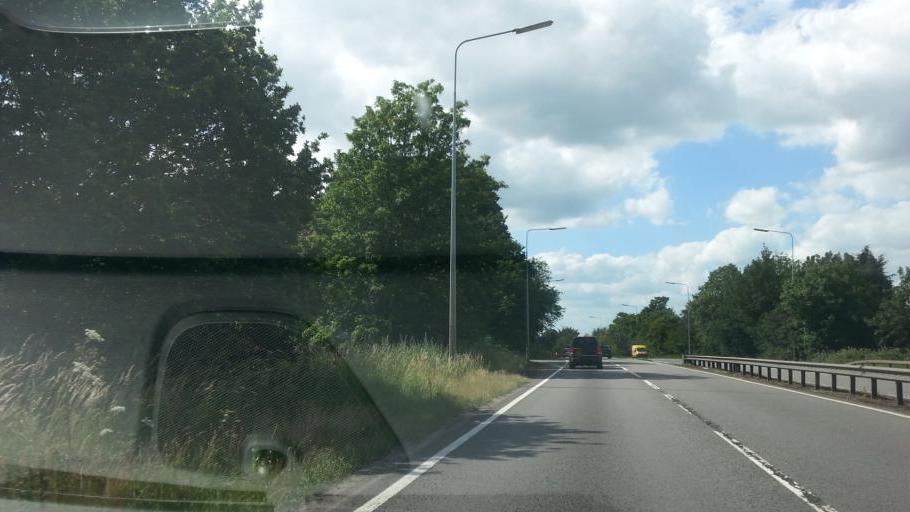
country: GB
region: England
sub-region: Central Bedfordshire
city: Biggleswade
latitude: 52.0742
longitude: -0.2474
